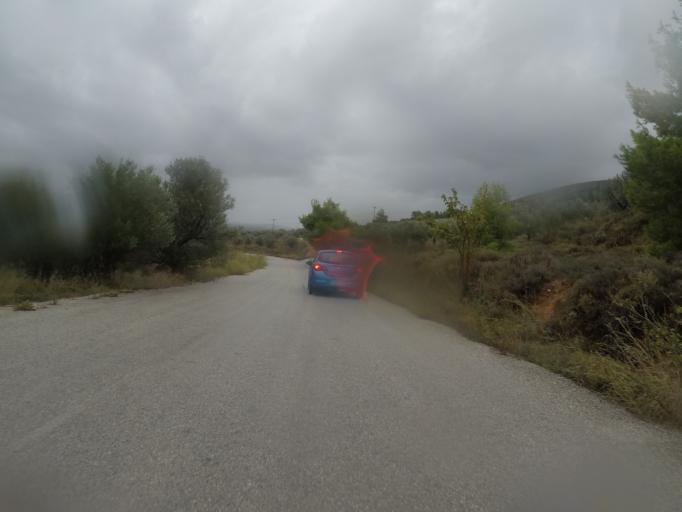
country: GR
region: Peloponnese
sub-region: Nomos Korinthias
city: Arkhaia Korinthos
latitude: 37.8986
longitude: 22.8803
